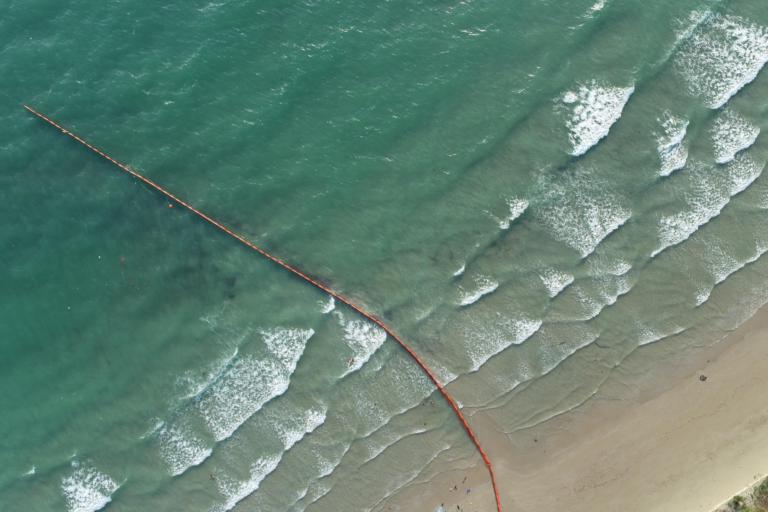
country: TH
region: Rayong
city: Rayong
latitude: 12.6036
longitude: 101.3969
